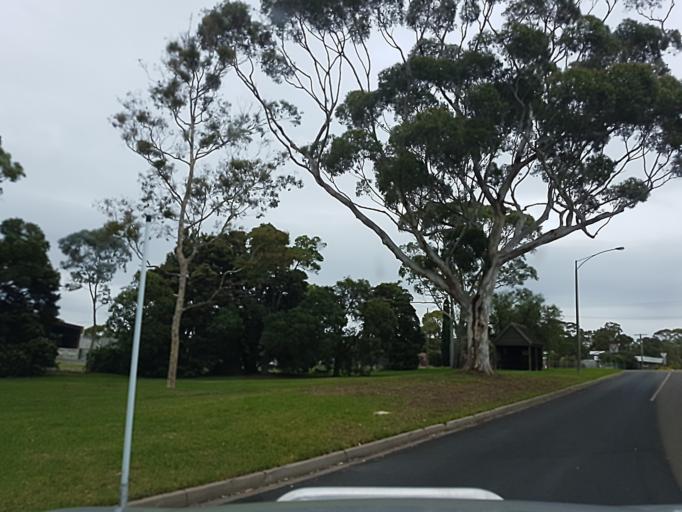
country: AU
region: Victoria
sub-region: Wellington
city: Sale
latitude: -38.1132
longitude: 147.0695
